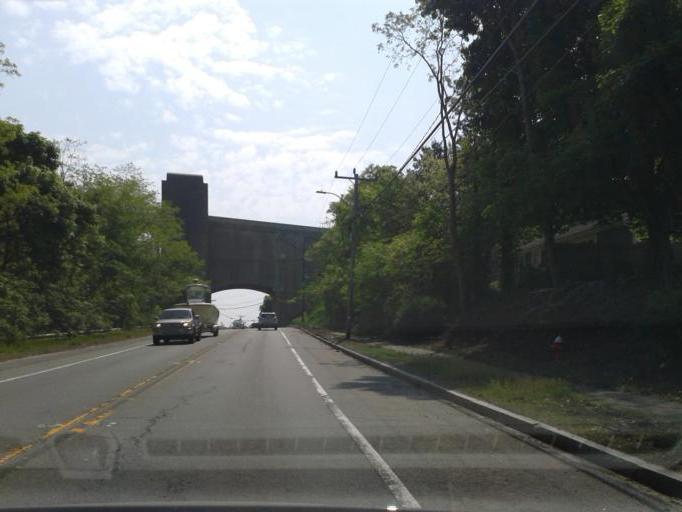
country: US
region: Massachusetts
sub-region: Barnstable County
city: Sagamore
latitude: 41.7742
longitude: -70.5453
